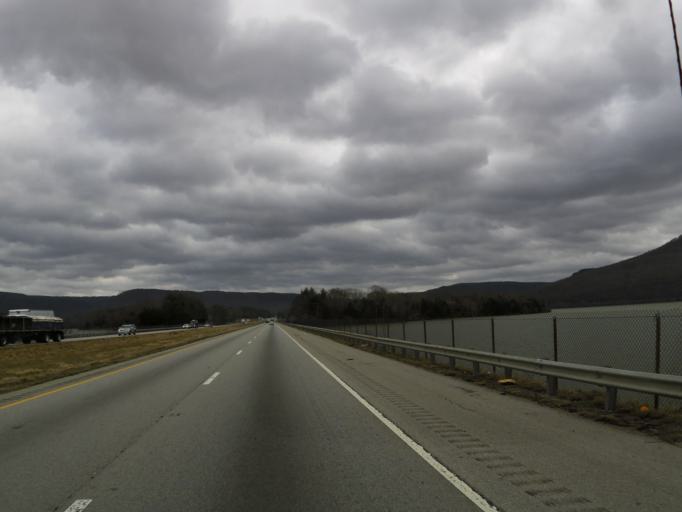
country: US
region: Tennessee
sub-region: Marion County
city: Jasper
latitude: 35.0282
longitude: -85.5683
